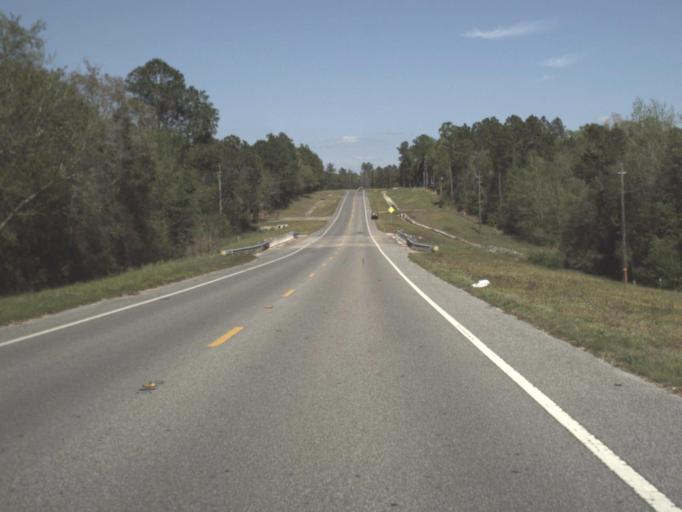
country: US
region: Florida
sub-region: Okaloosa County
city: Crestview
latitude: 30.7273
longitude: -86.6611
